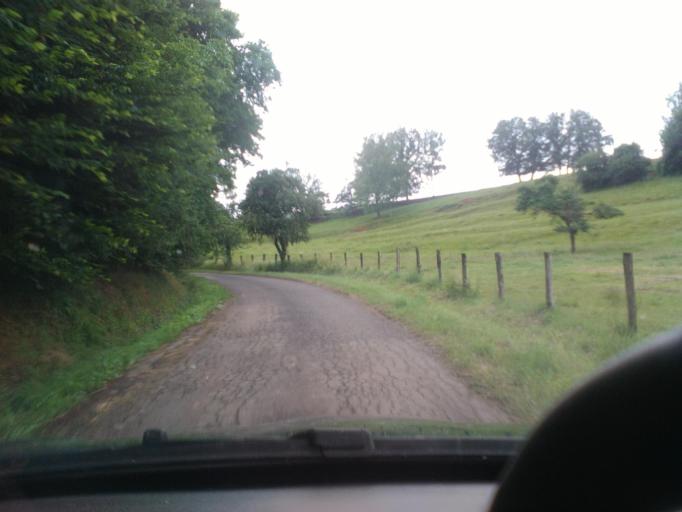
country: FR
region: Lorraine
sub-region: Departement des Vosges
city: Moyenmoutier
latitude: 48.3477
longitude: 6.9369
